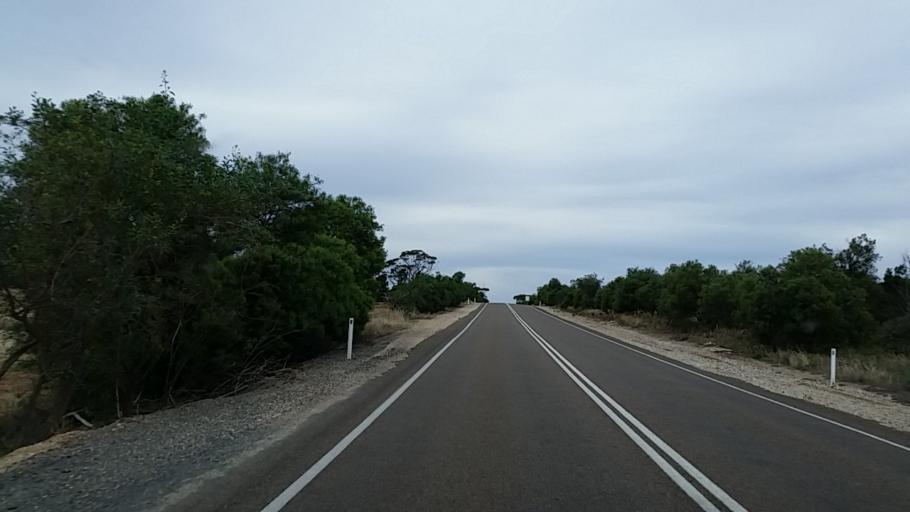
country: AU
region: South Australia
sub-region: Mid Murray
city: Mannum
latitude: -34.9312
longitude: 139.2424
